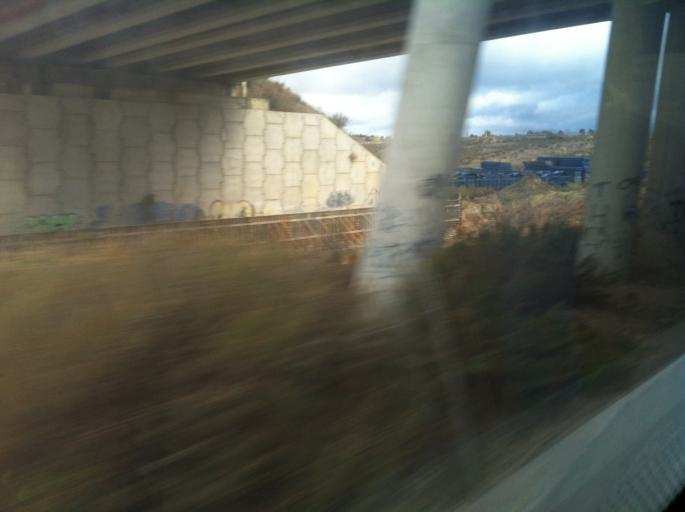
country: ES
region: Basque Country
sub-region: Provincia de Alava
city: Arminon
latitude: 42.7006
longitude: -2.9022
